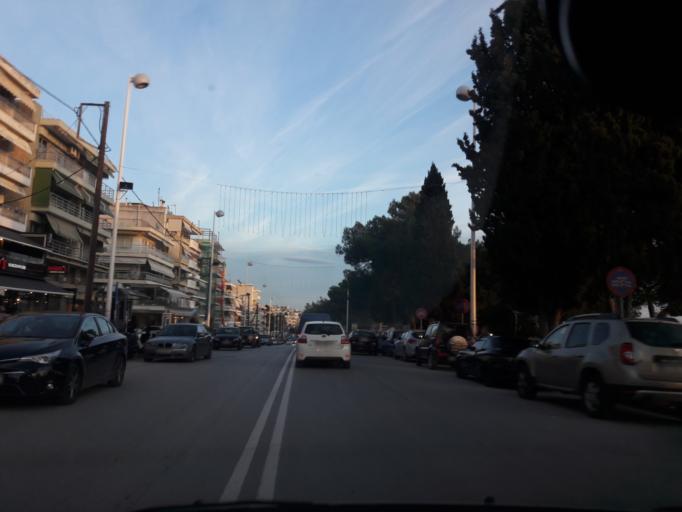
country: GR
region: Central Macedonia
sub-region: Nomos Thessalonikis
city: Kalamaria
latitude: 40.5749
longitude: 22.9486
